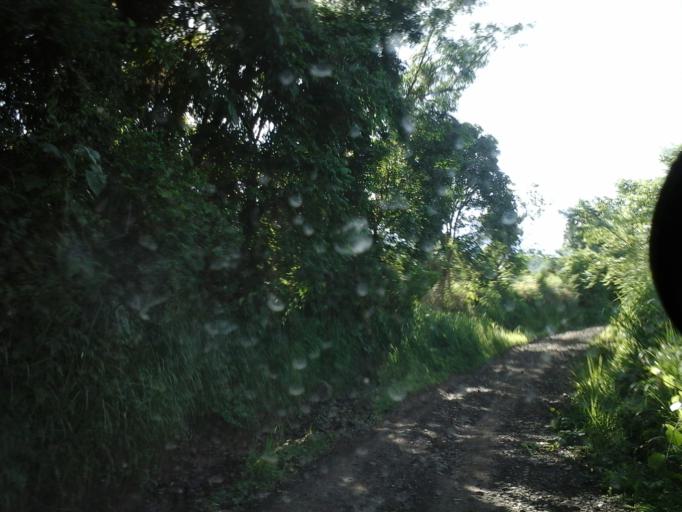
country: CO
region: Cesar
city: San Diego
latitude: 10.2688
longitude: -73.0815
